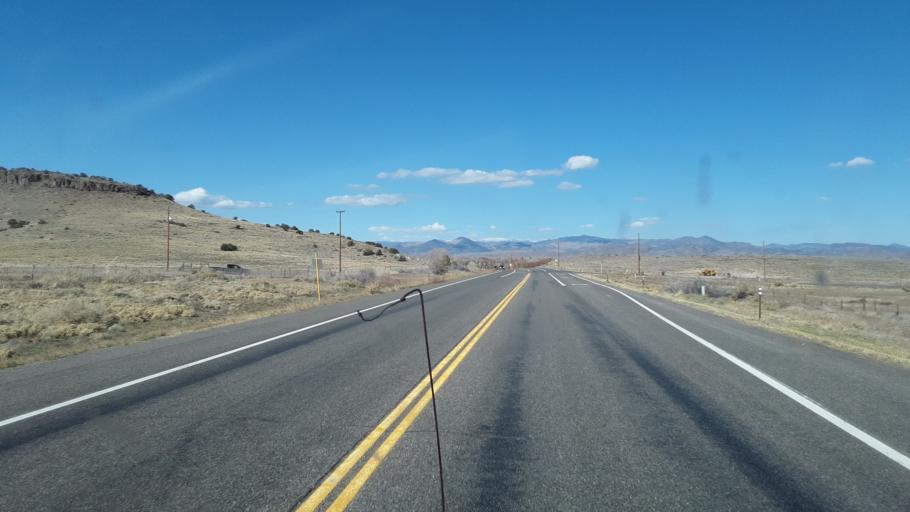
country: US
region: Colorado
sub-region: Rio Grande County
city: Del Norte
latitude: 37.6475
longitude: -106.2720
